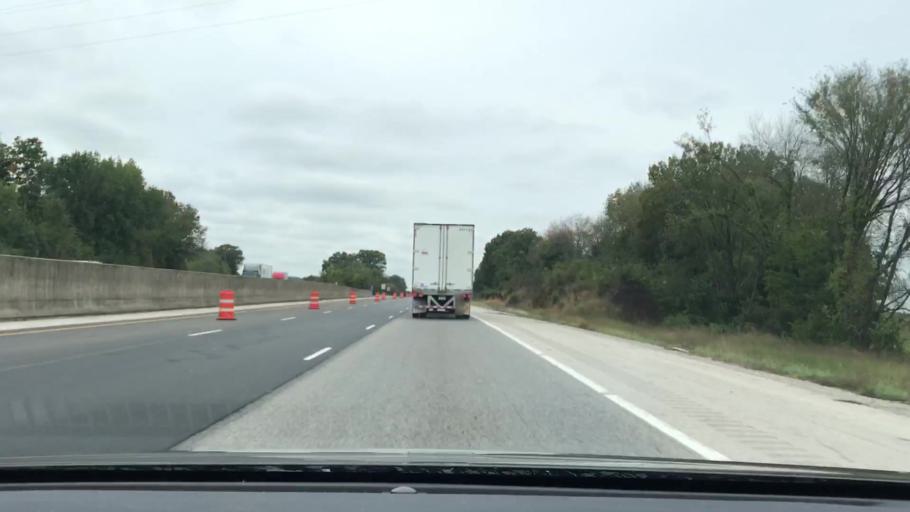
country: US
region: Kentucky
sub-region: Barren County
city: Cave City
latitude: 37.0557
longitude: -86.1286
